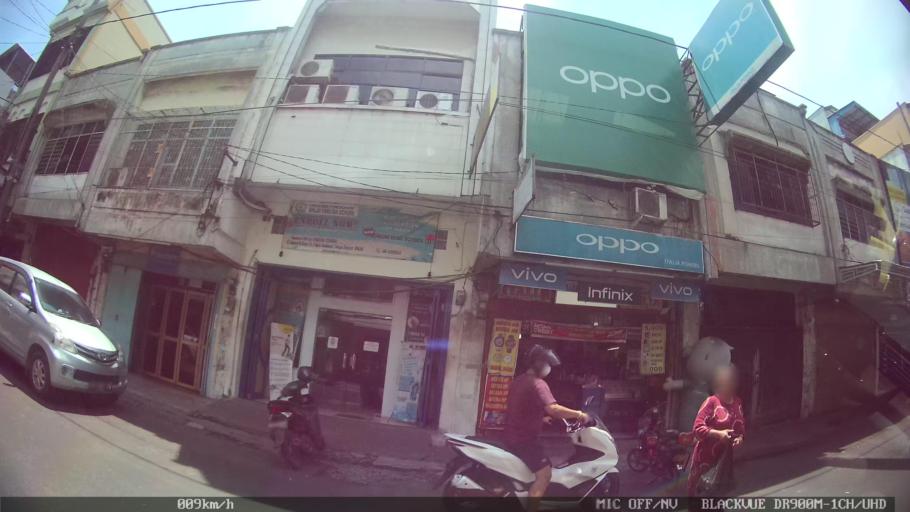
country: ID
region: North Sumatra
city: Binjai
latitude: 3.6074
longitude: 98.4897
